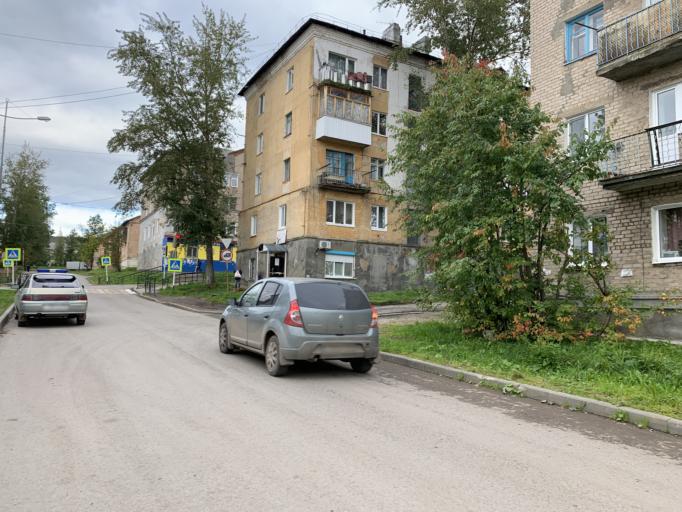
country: RU
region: Perm
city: Gubakha
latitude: 58.8429
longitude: 57.5494
